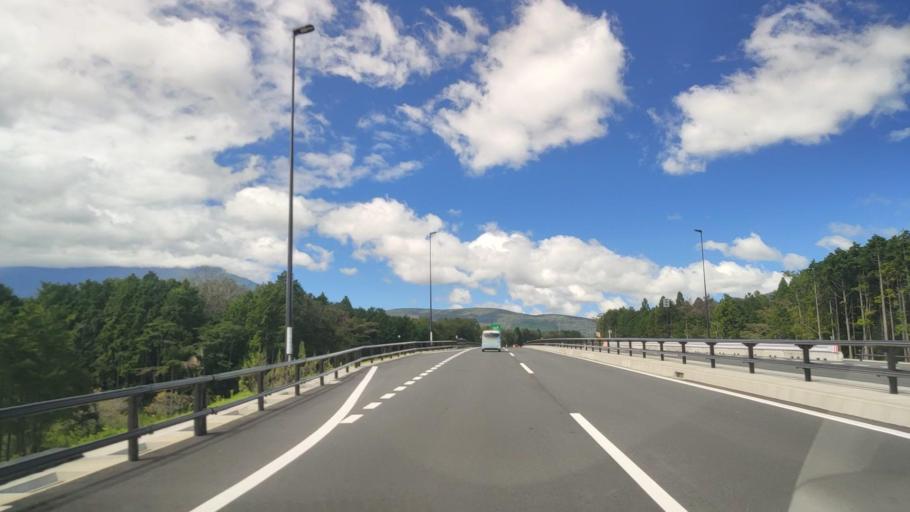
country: JP
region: Shizuoka
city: Gotemba
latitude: 35.3330
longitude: 138.8954
